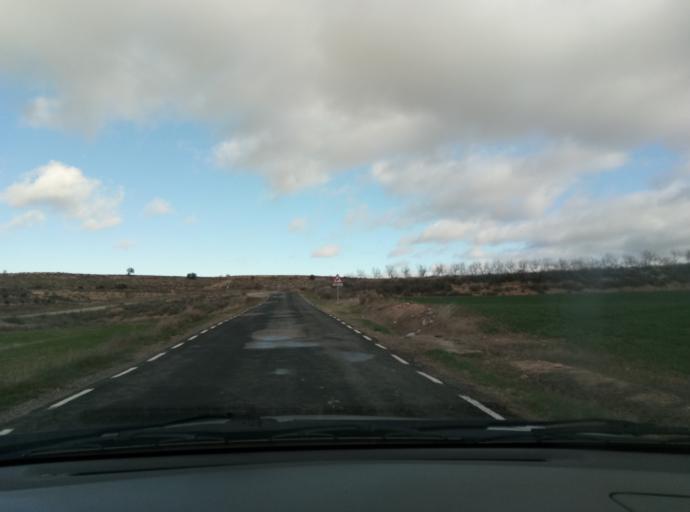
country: ES
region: Catalonia
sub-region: Provincia de Lleida
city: Verdu
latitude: 41.6075
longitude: 1.1046
